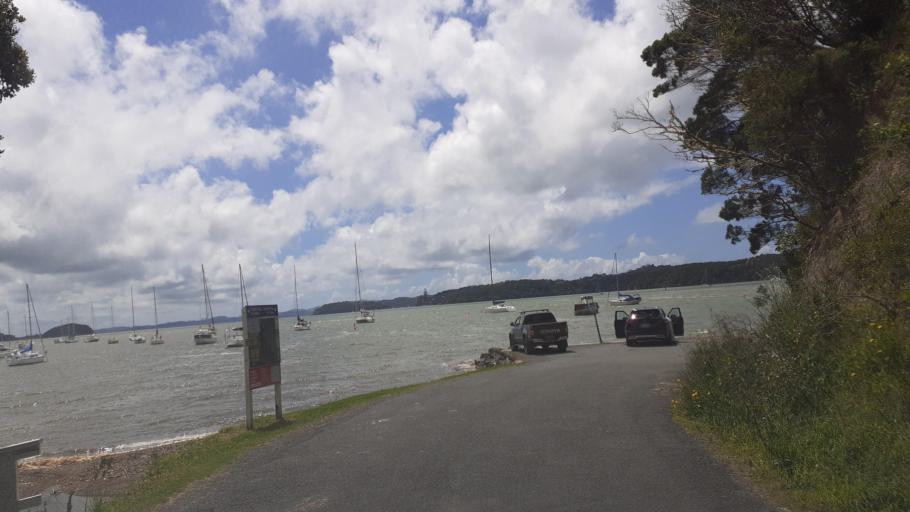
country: NZ
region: Northland
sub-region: Far North District
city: Paihia
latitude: -35.3077
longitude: 174.1116
